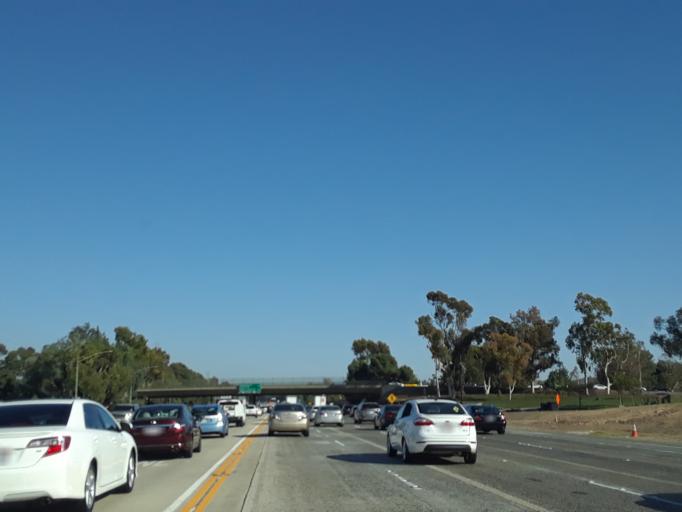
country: US
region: California
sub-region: Orange County
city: Irvine
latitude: 33.6703
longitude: -117.8253
